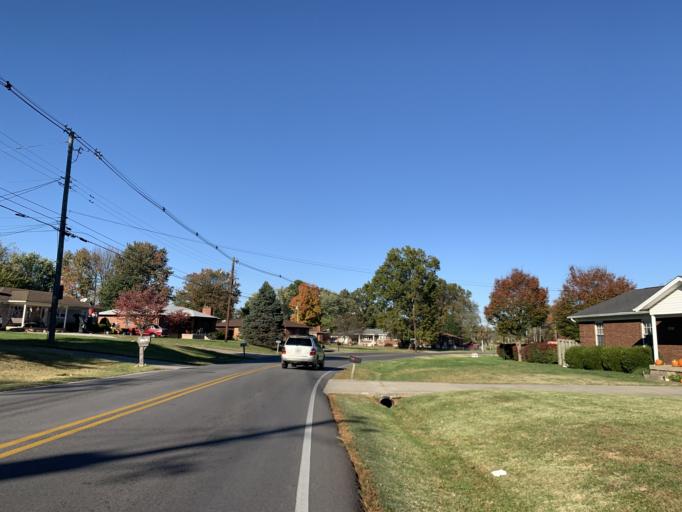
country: US
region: Kentucky
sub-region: Jefferson County
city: Pleasure Ridge Park
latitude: 38.1638
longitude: -85.8442
